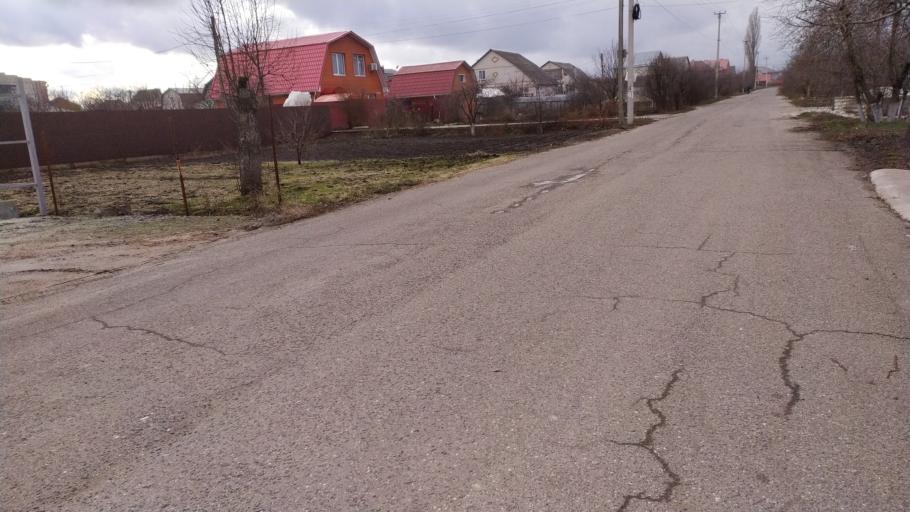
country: RU
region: Kursk
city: Kursk
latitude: 51.6399
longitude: 36.1453
